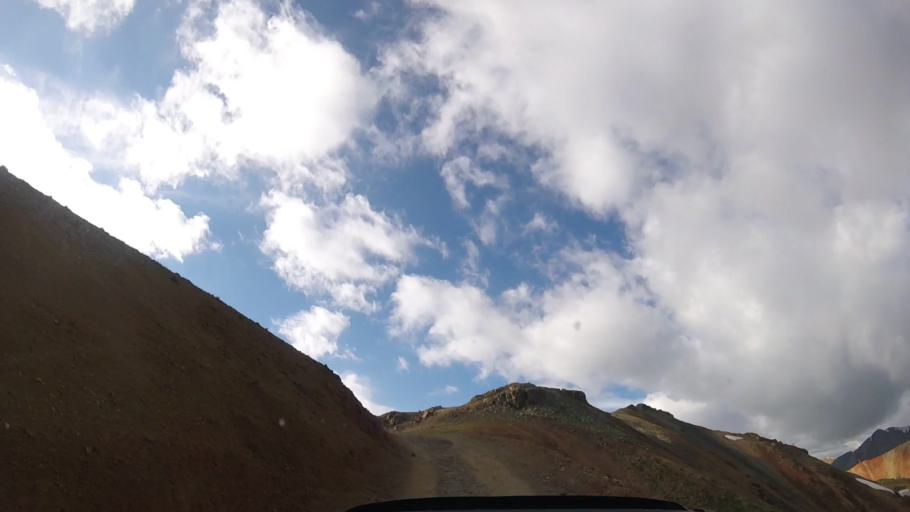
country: US
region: Colorado
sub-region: San Juan County
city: Silverton
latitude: 37.9071
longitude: -107.6632
